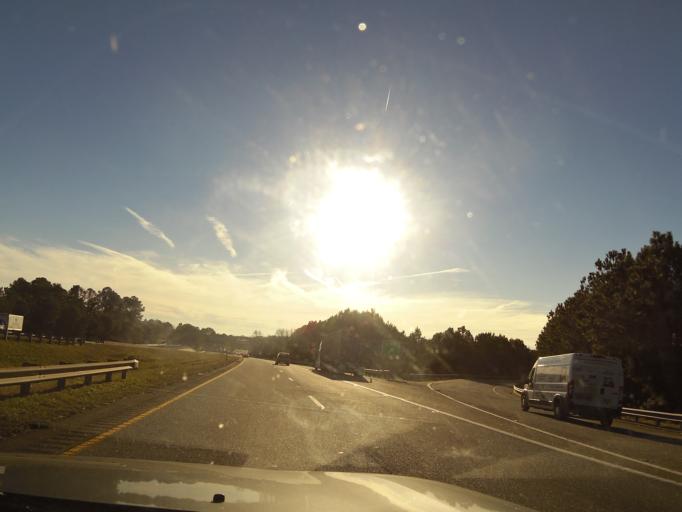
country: US
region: Virginia
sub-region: City of Suffolk
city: South Suffolk
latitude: 36.7299
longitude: -76.6295
